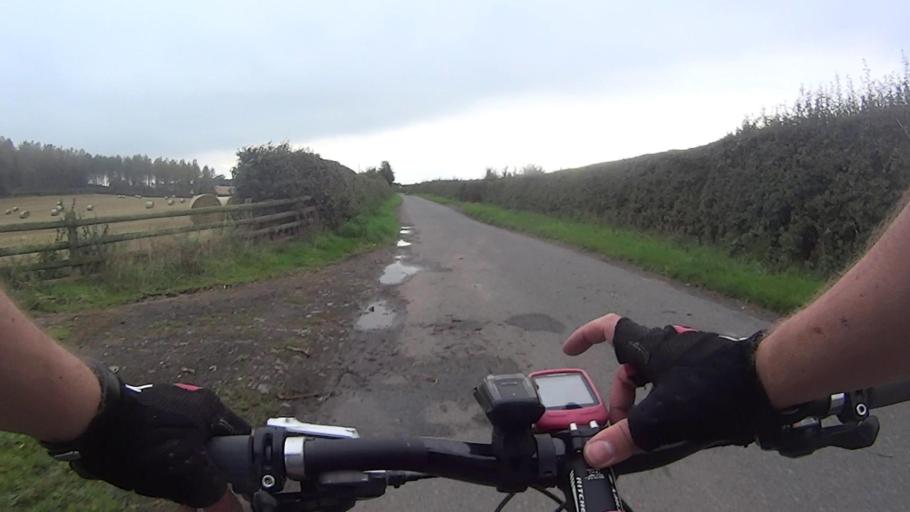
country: GB
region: England
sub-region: Worcestershire
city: Tenbury Wells
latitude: 52.3136
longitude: -2.5727
